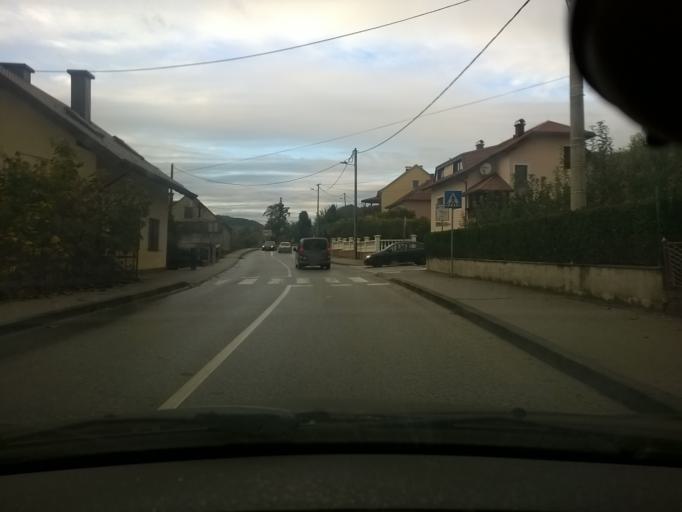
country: HR
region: Krapinsko-Zagorska
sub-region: Grad Krapina
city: Krapina
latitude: 46.1579
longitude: 15.8757
